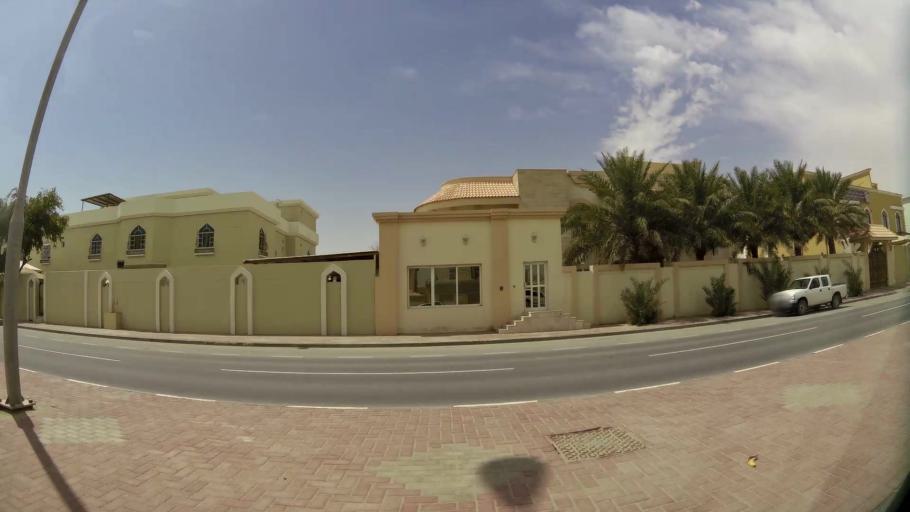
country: QA
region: Baladiyat ar Rayyan
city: Ar Rayyan
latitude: 25.2920
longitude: 51.4140
